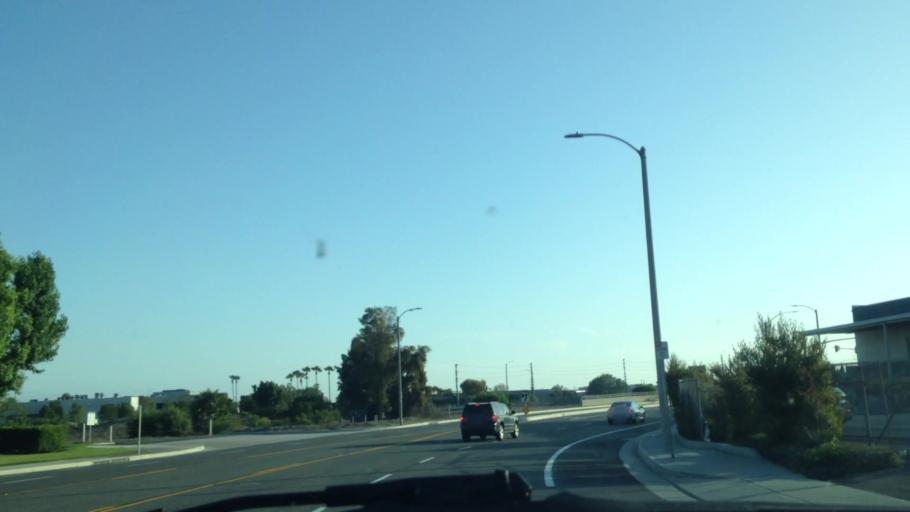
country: US
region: California
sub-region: Orange County
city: Tustin
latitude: 33.7229
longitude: -117.8334
